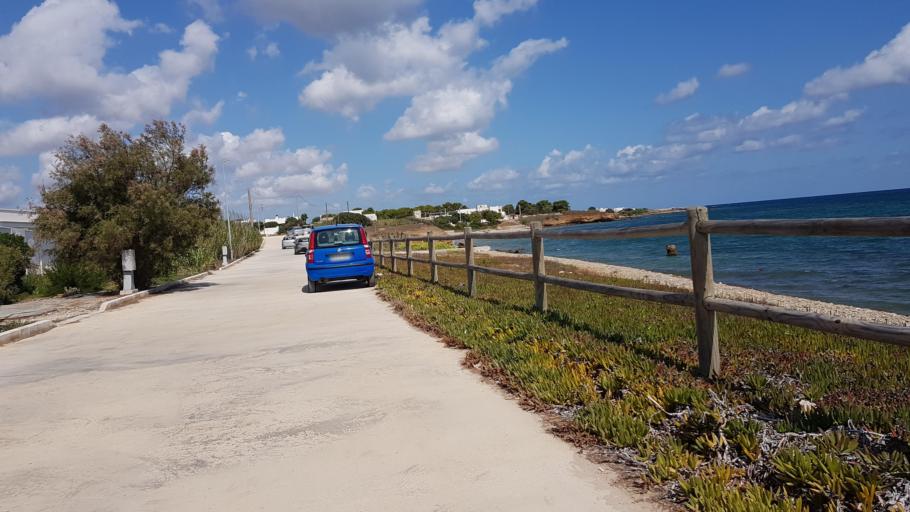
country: IT
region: Apulia
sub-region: Provincia di Brindisi
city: Torchiarolo
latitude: 40.5257
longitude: 18.0803
